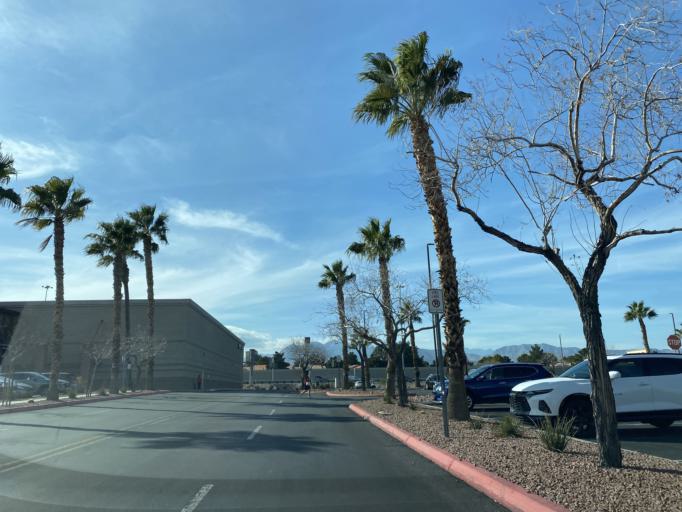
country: US
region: Nevada
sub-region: Clark County
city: Spring Valley
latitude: 36.2012
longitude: -115.2427
